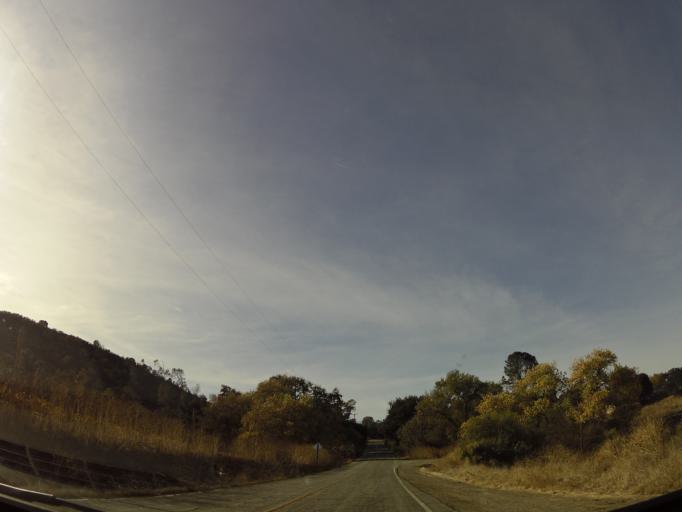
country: US
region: California
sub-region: San Benito County
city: Ridgemark
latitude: 36.6768
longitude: -121.2841
